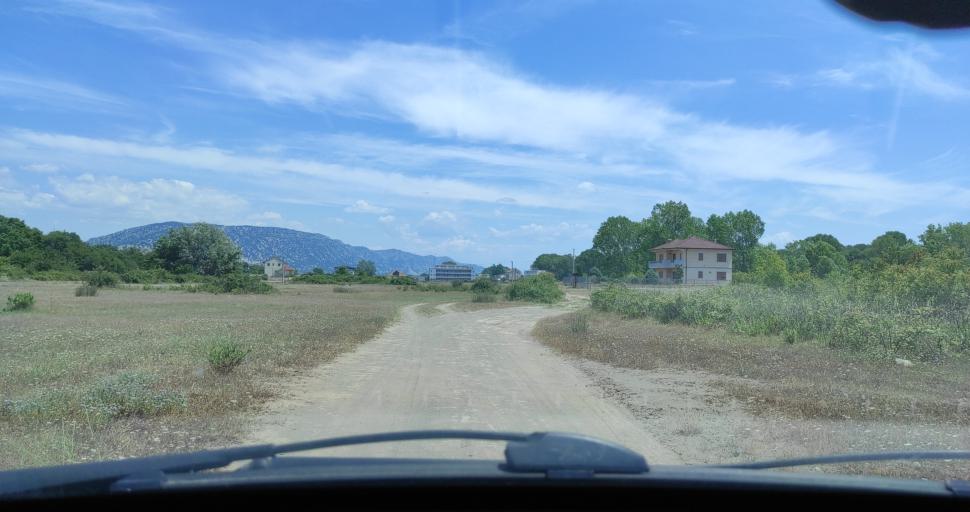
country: AL
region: Shkoder
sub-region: Rrethi i Shkodres
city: Velipoje
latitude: 41.8701
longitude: 19.3950
